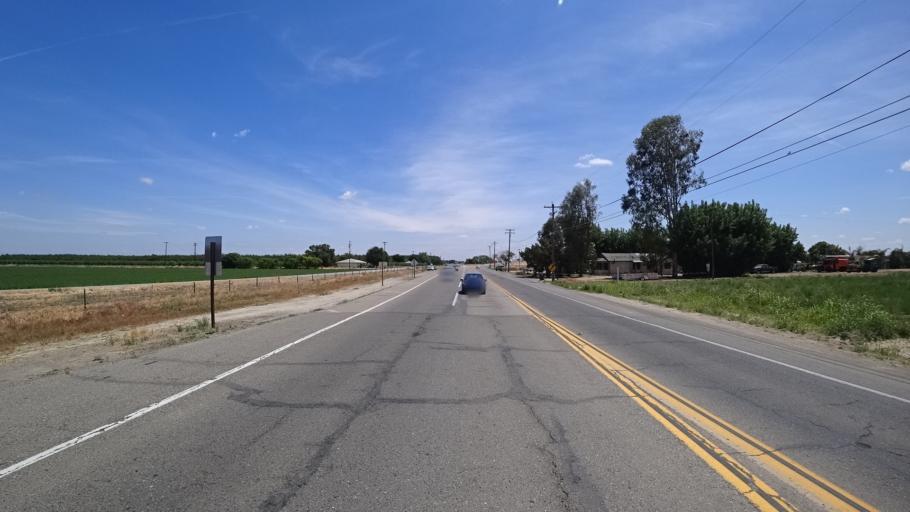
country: US
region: California
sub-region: Kings County
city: Lemoore
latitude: 36.2983
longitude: -119.7600
